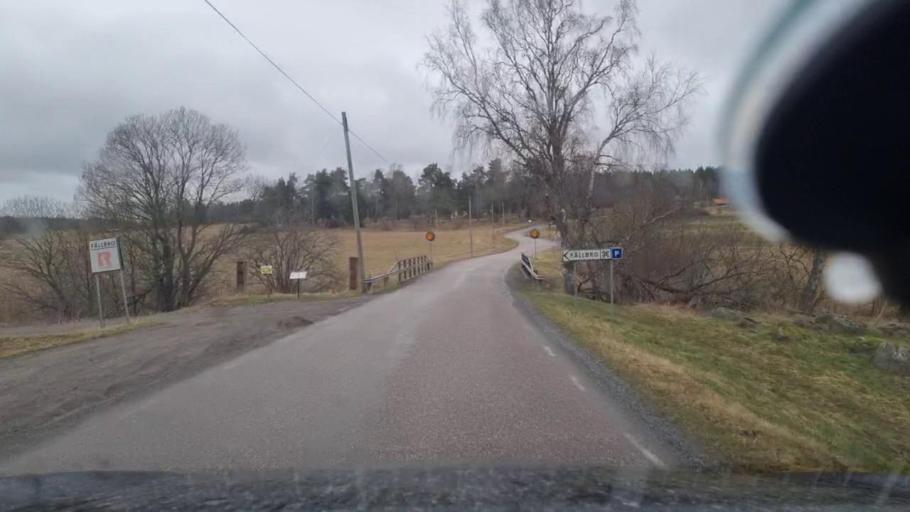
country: SE
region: Stockholm
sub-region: Taby Kommun
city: Taby
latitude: 59.4806
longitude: 18.0149
